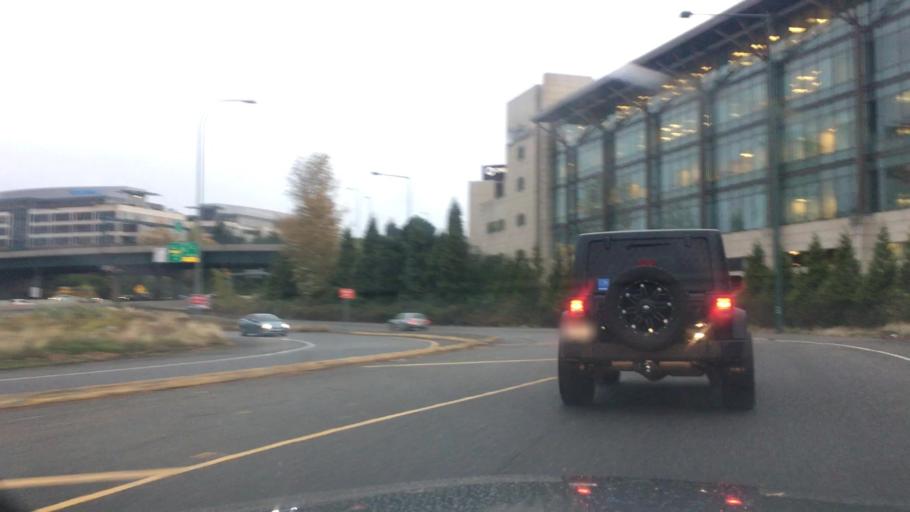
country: US
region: Washington
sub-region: King County
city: Bellevue
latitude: 47.6176
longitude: -122.1869
